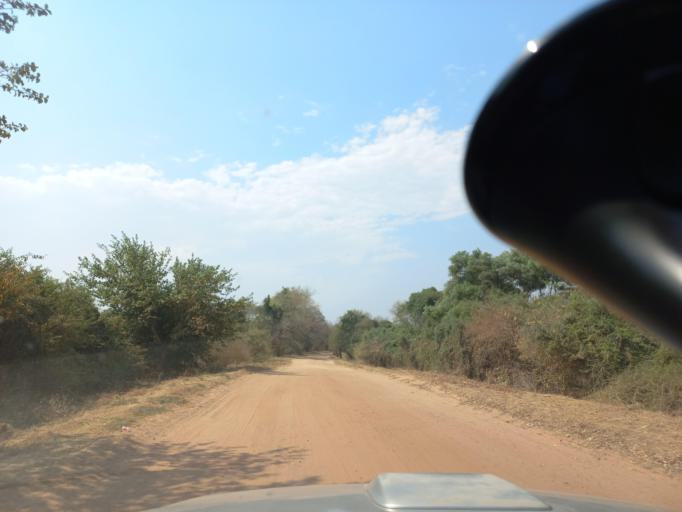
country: ZW
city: Chirundu
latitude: -15.9303
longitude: 28.8714
